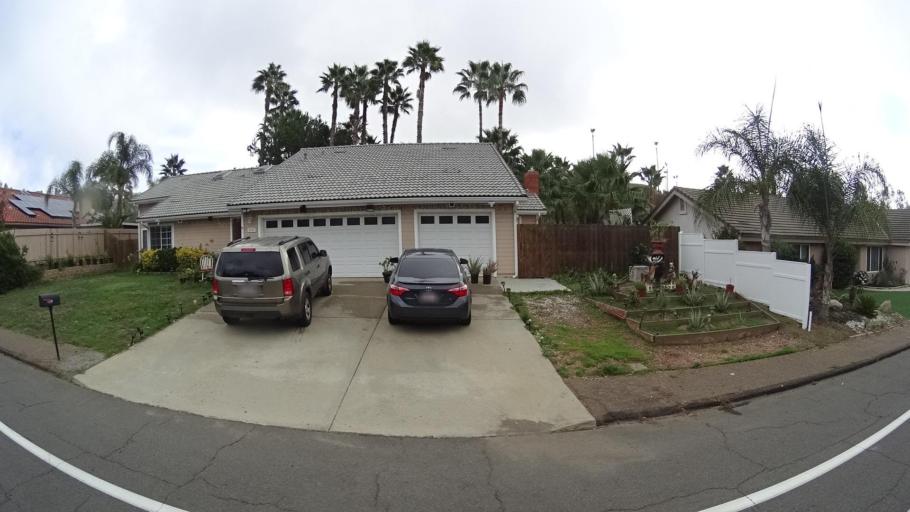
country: US
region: California
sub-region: San Diego County
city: Granite Hills
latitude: 32.7718
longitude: -116.9075
